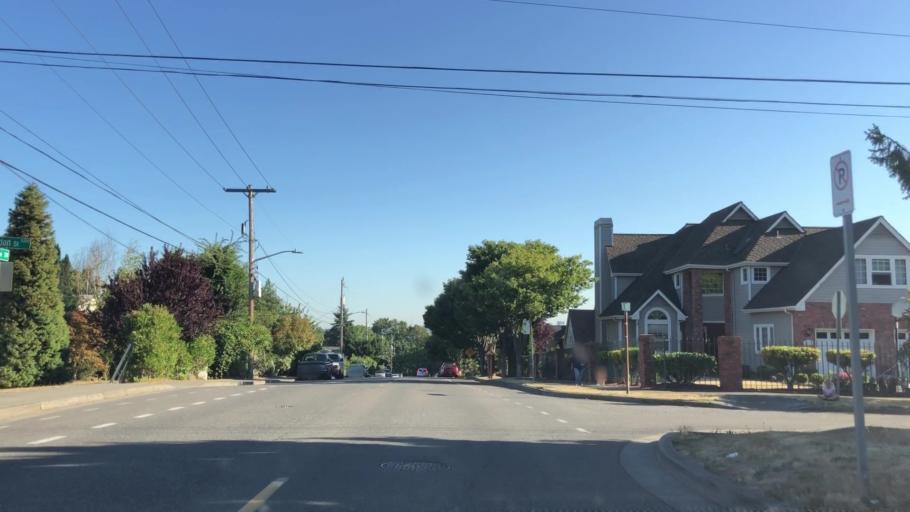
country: US
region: Washington
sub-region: King County
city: White Center
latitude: 47.5536
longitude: -122.3549
